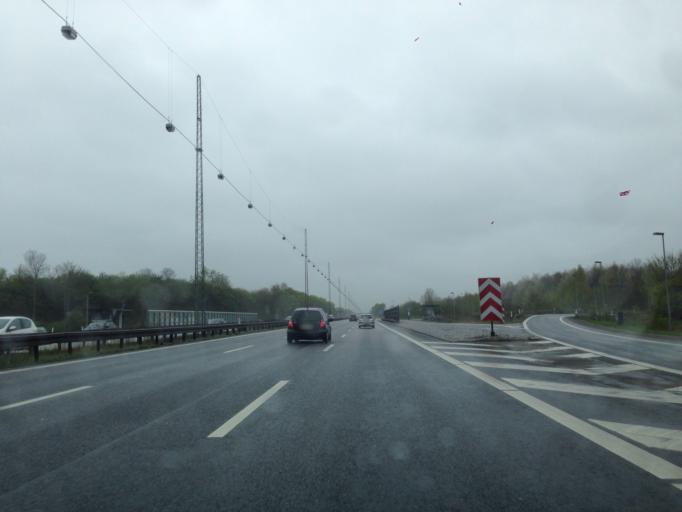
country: DK
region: Capital Region
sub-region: Lyngby-Tarbaek Kommune
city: Kongens Lyngby
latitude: 55.7966
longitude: 12.5323
